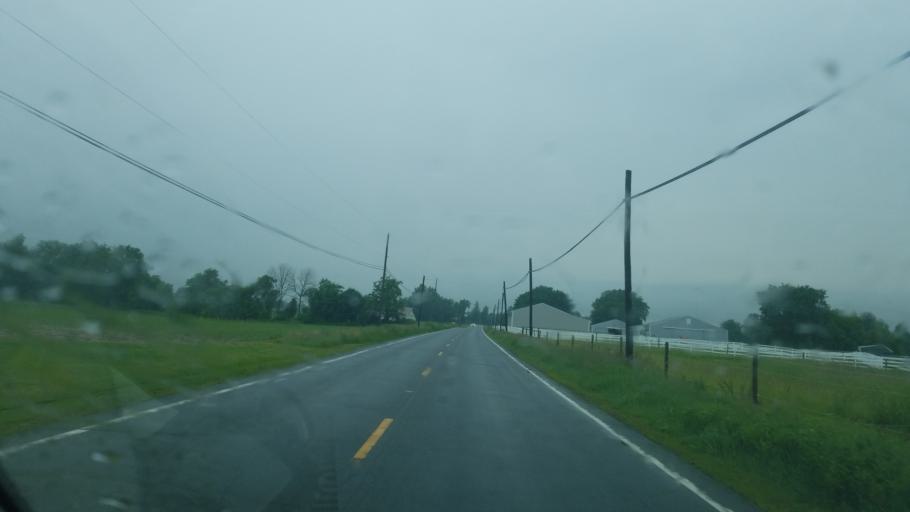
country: US
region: Ohio
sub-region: Richland County
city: Shelby
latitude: 40.9258
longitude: -82.6592
